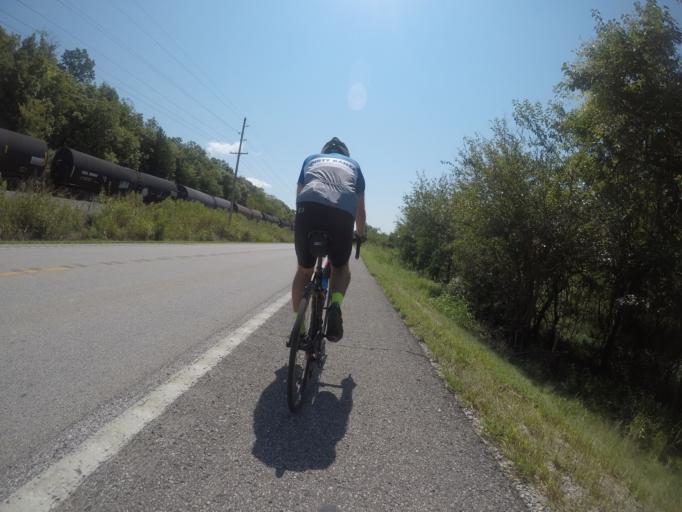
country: US
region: Missouri
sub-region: Platte County
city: Weston
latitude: 39.4772
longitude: -94.9869
